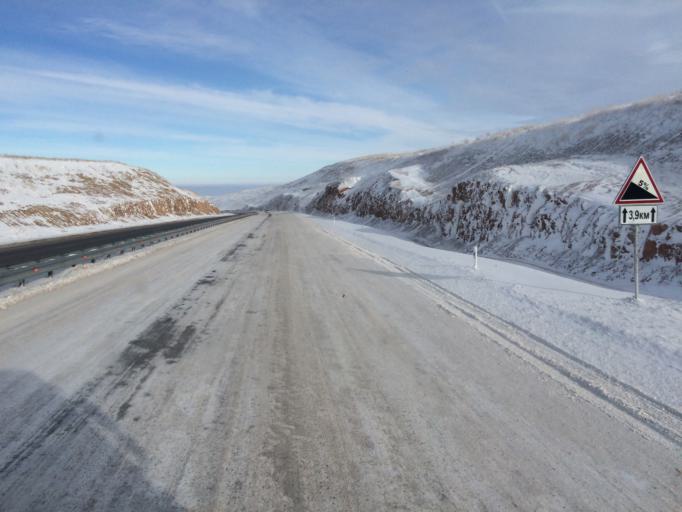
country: KZ
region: Zhambyl
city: Georgiyevka
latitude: 43.4066
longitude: 74.8616
